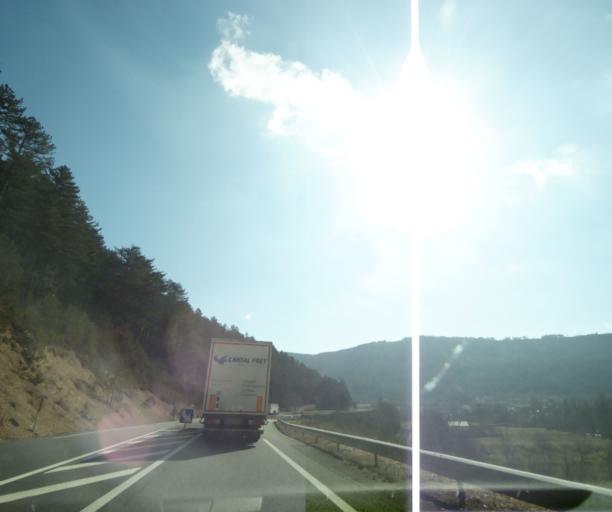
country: FR
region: Languedoc-Roussillon
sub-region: Departement de la Lozere
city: Mende
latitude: 44.4853
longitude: 3.4245
